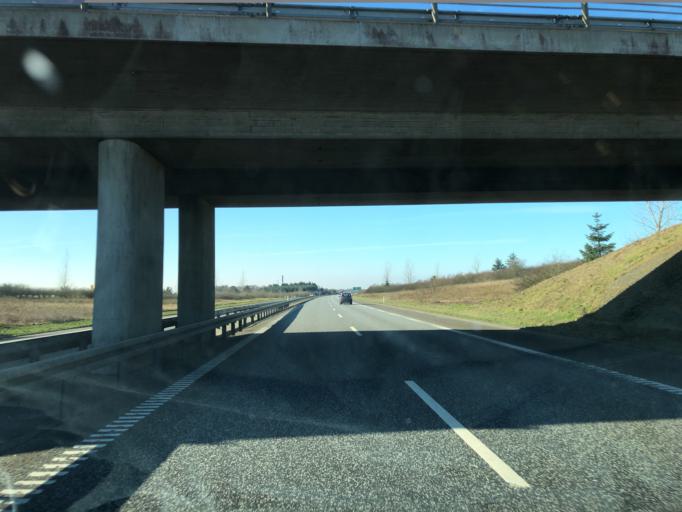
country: DK
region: Central Jutland
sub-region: Herning Kommune
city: Hammerum
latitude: 56.1204
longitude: 9.0495
